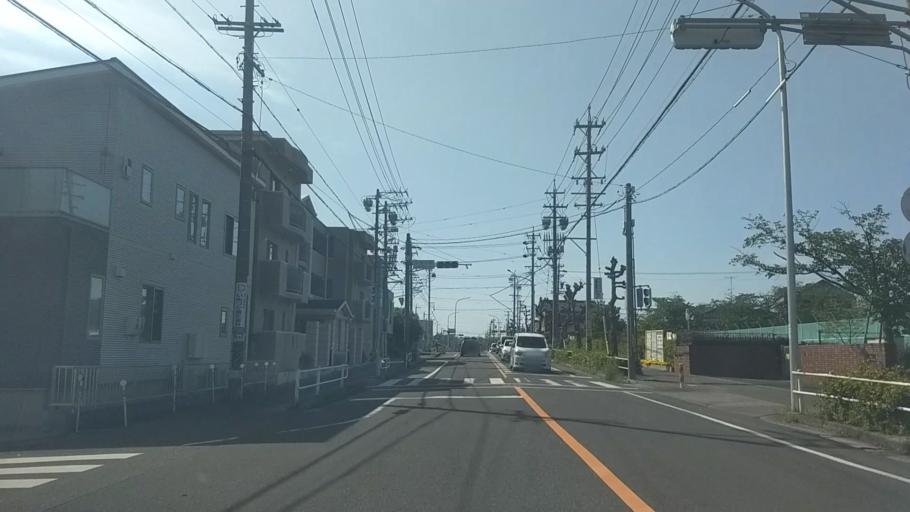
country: JP
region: Aichi
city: Anjo
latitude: 34.9645
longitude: 137.0843
